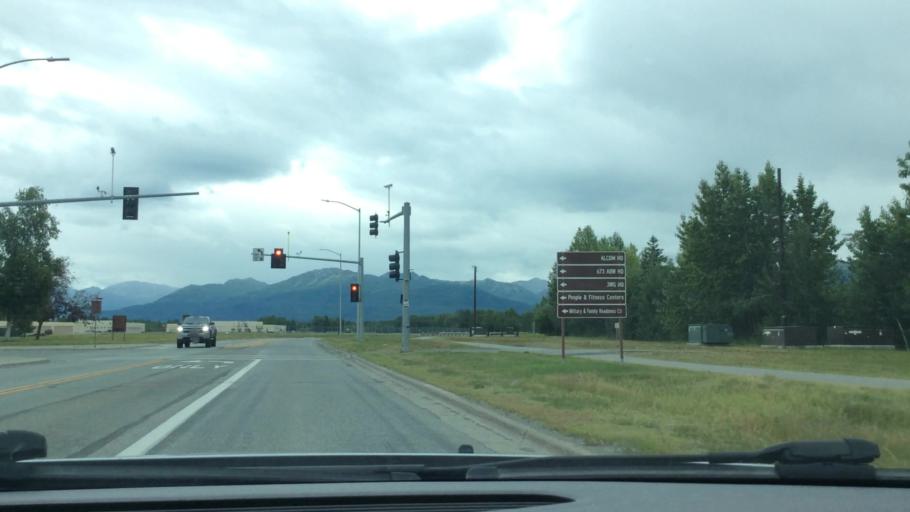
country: US
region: Alaska
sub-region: Anchorage Municipality
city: Anchorage
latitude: 61.2395
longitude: -149.8017
